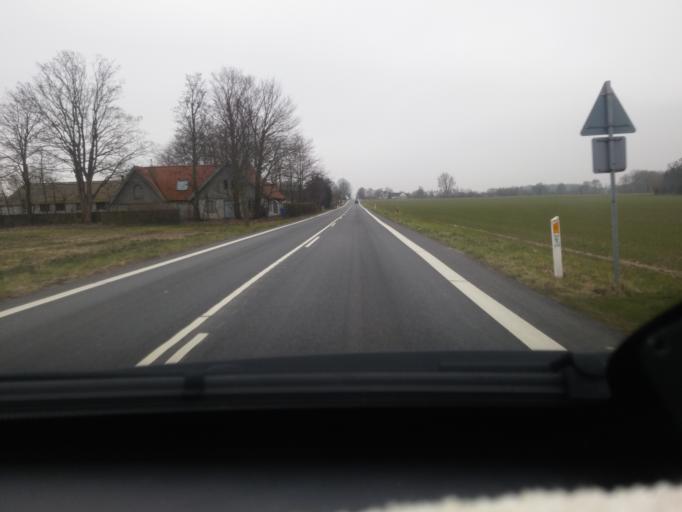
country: DK
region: South Denmark
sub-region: Nyborg Kommune
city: Ullerslev
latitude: 55.3992
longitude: 10.7304
